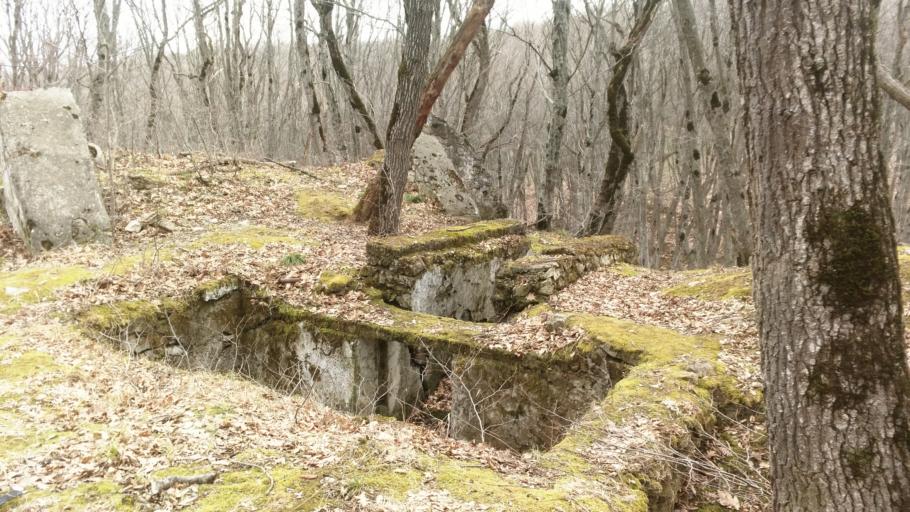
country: RU
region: Stavropol'skiy
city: Zheleznovodsk
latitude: 44.1270
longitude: 43.0222
